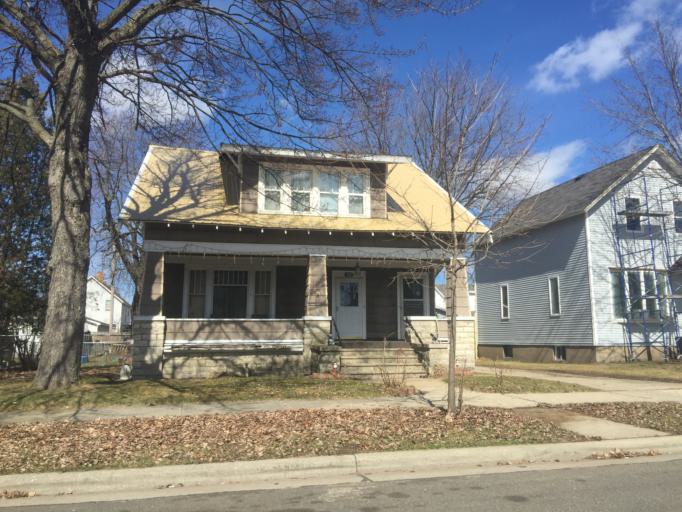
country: US
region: Wisconsin
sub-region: Marinette County
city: Marinette
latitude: 45.0954
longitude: -87.6257
